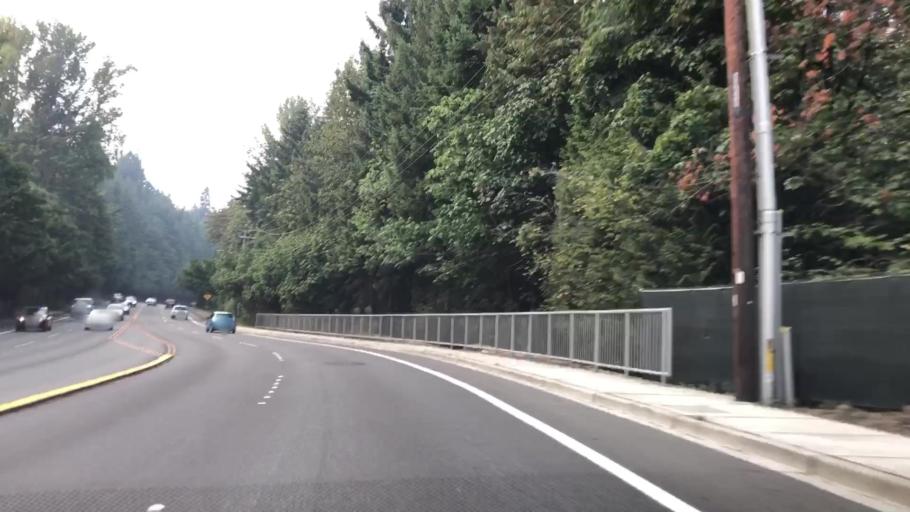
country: US
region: Washington
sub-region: King County
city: Newcastle
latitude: 47.5444
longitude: -122.1643
